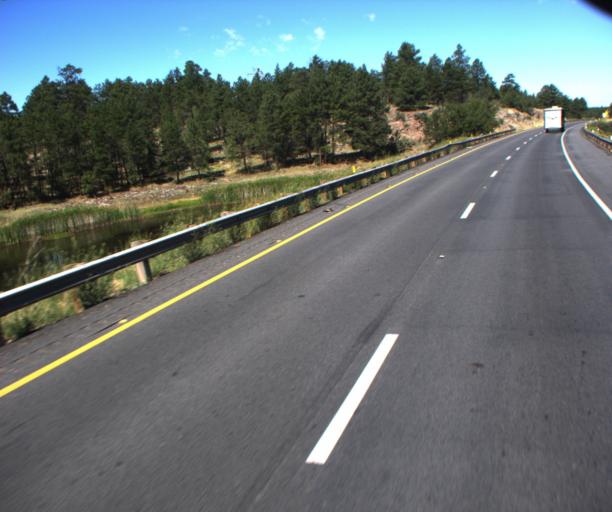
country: US
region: Arizona
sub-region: Coconino County
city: Williams
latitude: 35.2198
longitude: -112.2854
